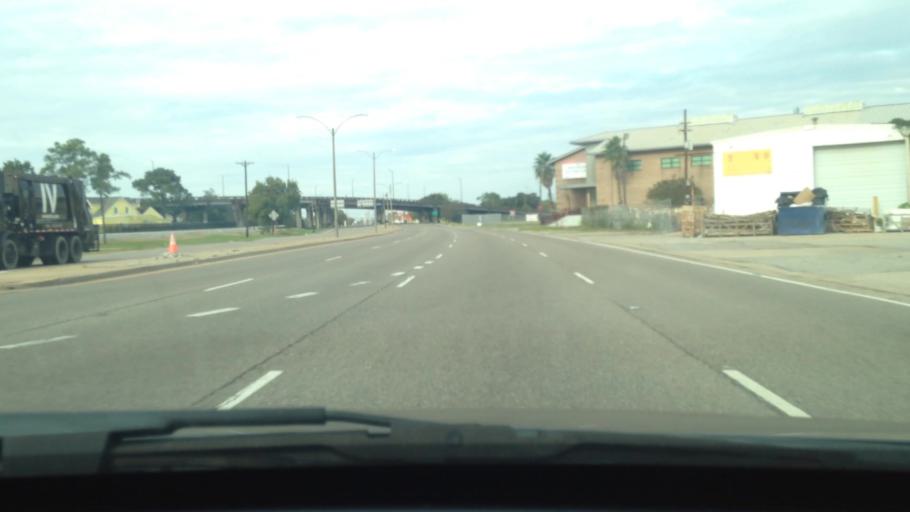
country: US
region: Louisiana
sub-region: Jefferson Parish
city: Jefferson
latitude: 29.9713
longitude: -90.1137
